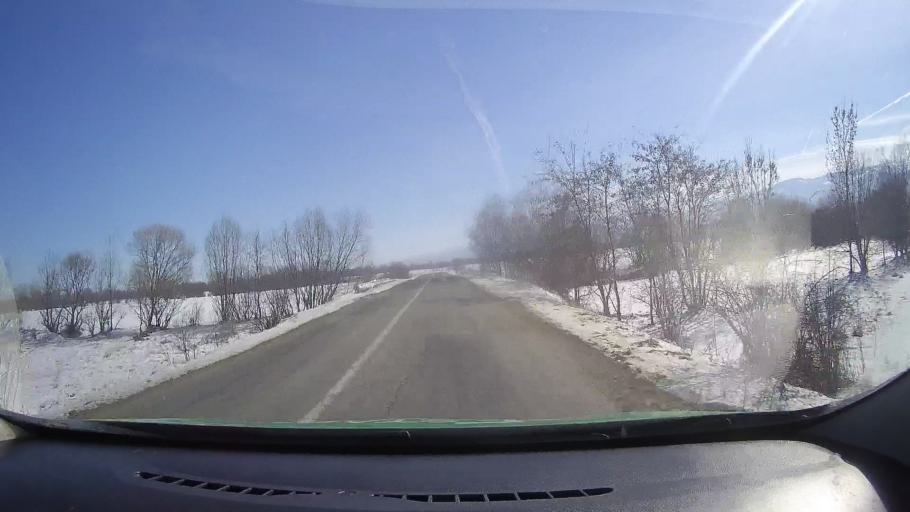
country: RO
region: Brasov
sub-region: Comuna Recea
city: Recea
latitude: 45.7295
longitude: 24.9697
